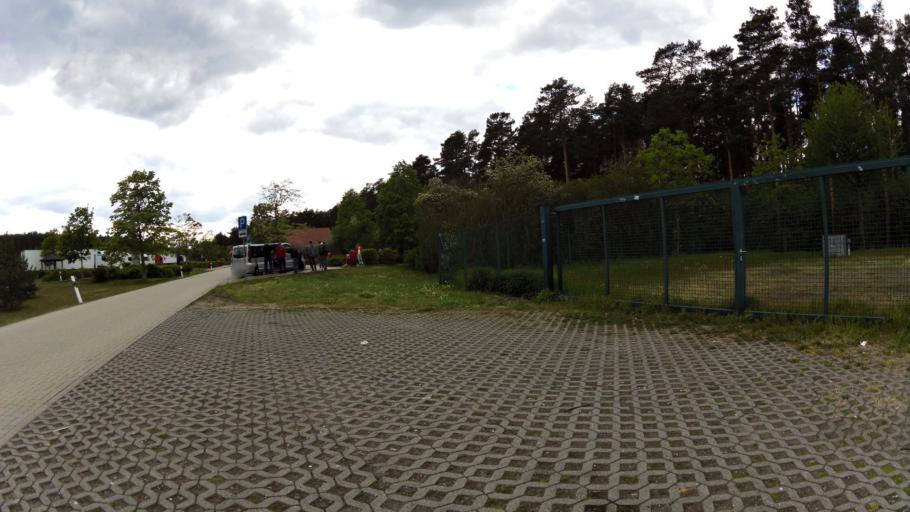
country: DE
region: Brandenburg
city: Wildau
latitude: 52.3239
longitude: 13.7066
